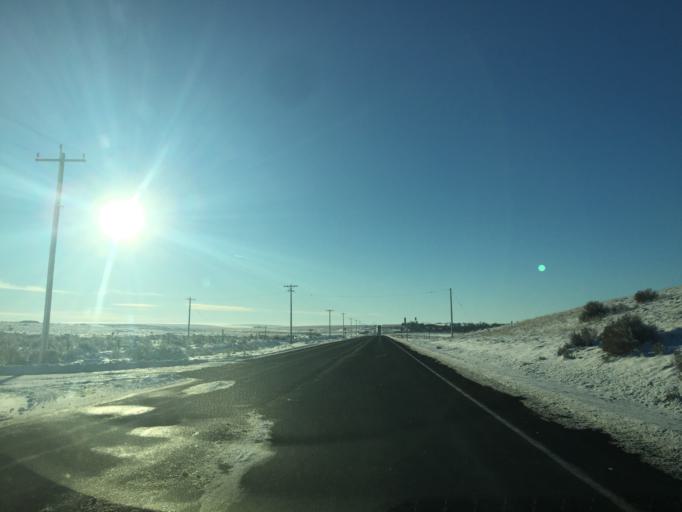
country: US
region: Washington
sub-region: Okanogan County
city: Coulee Dam
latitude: 47.7144
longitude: -118.9147
